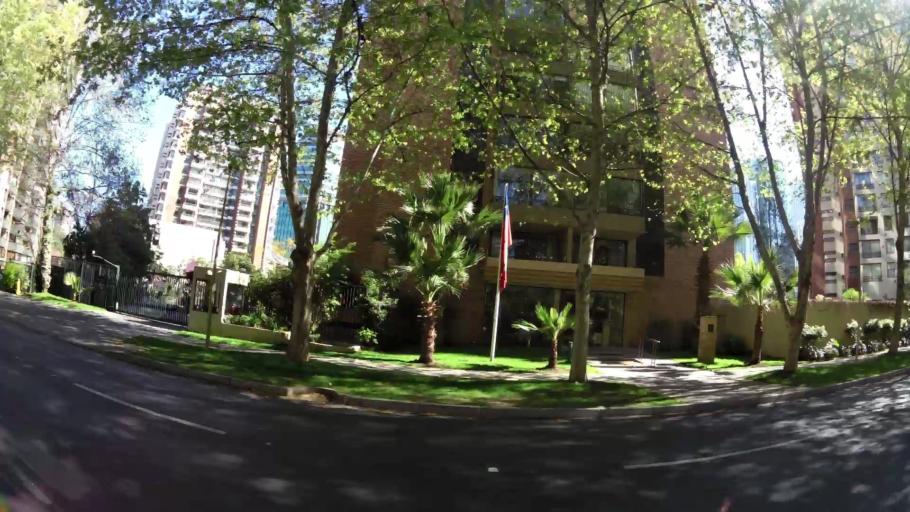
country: CL
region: Santiago Metropolitan
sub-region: Provincia de Santiago
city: Villa Presidente Frei, Nunoa, Santiago, Chile
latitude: -33.4077
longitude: -70.5754
